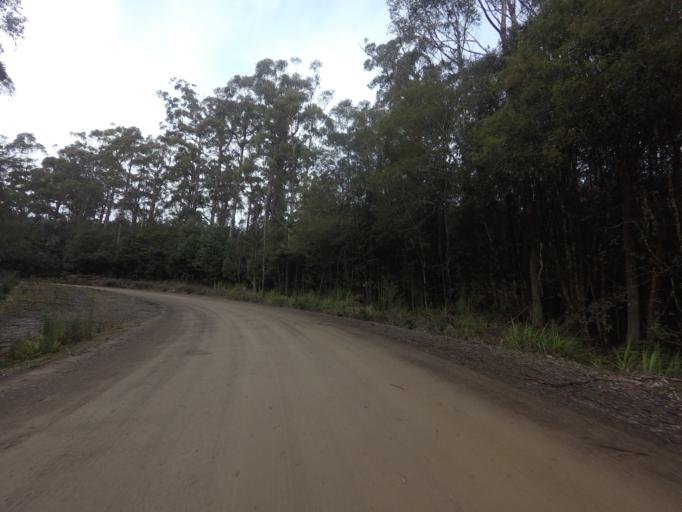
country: AU
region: Tasmania
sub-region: Huon Valley
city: Geeveston
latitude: -43.5070
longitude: 146.8757
